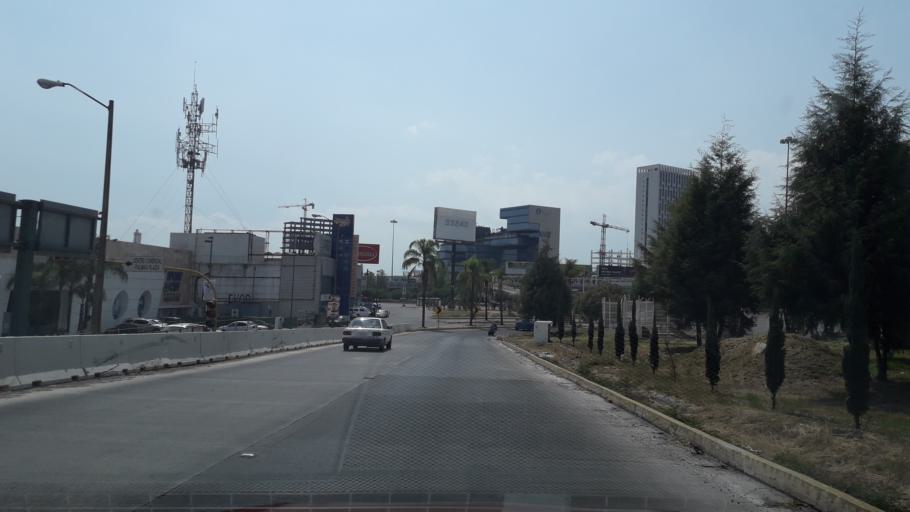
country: MX
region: Puebla
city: Puebla
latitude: 19.0277
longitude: -98.2321
